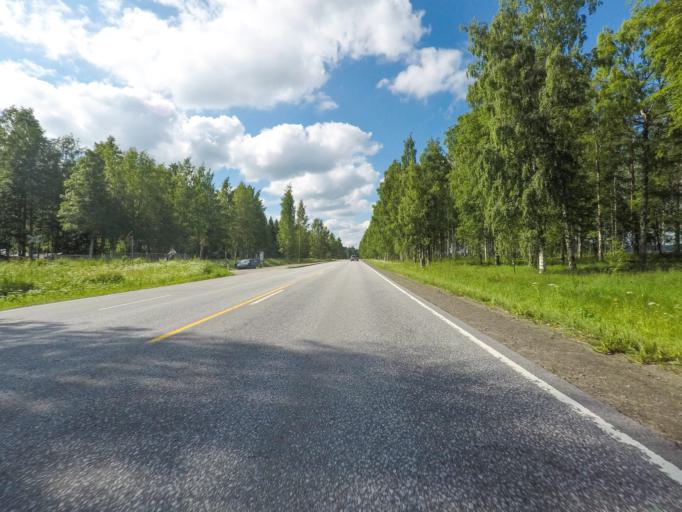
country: FI
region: Southern Savonia
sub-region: Savonlinna
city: Kerimaeki
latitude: 61.8081
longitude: 29.2751
